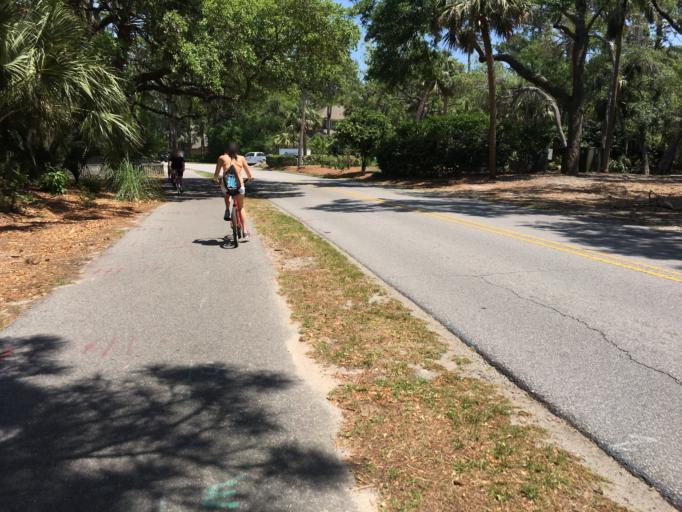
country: US
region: South Carolina
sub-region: Beaufort County
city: Hilton Head Island
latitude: 32.1154
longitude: -80.8091
